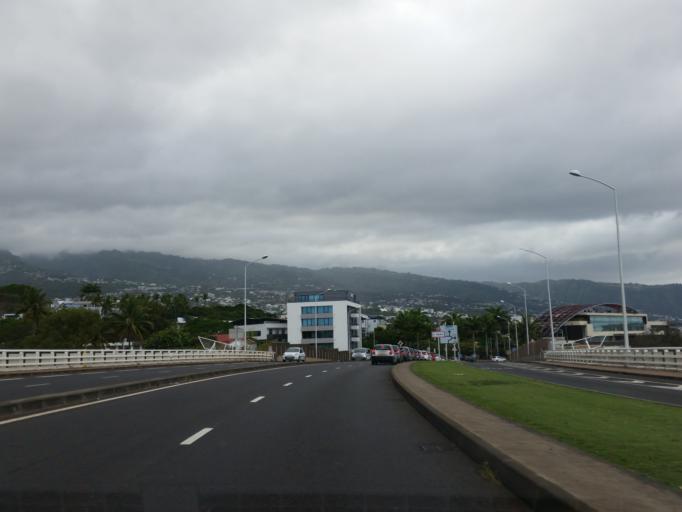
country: RE
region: Reunion
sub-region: Reunion
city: Sainte-Marie
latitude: -20.9020
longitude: 55.5048
